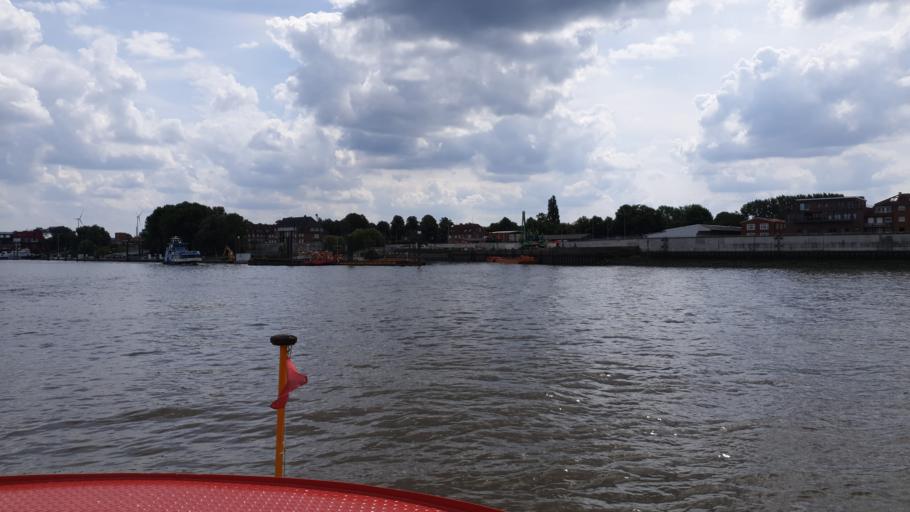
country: DE
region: Hamburg
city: Altona
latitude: 53.5399
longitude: 9.8764
